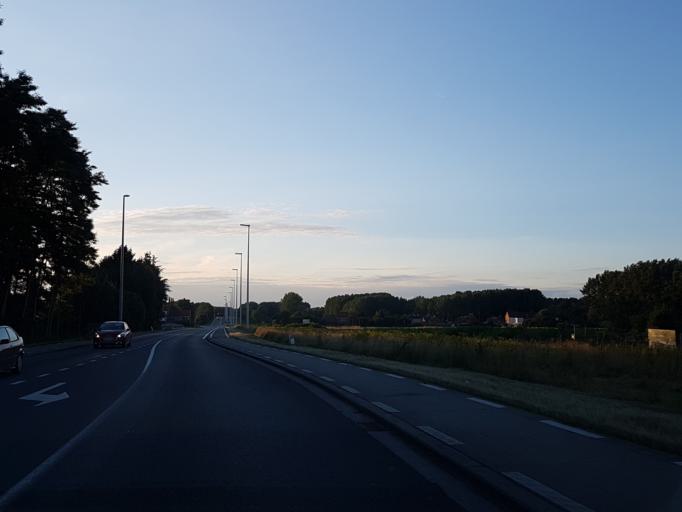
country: BE
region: Flanders
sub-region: Provincie Oost-Vlaanderen
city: Hamme
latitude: 51.0976
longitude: 4.1495
